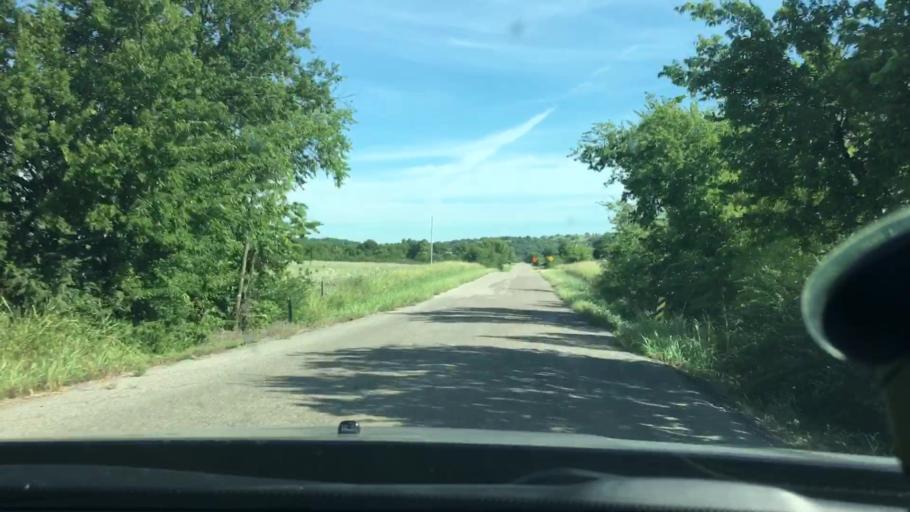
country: US
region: Oklahoma
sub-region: Carter County
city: Lone Grove
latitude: 34.3275
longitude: -97.2825
